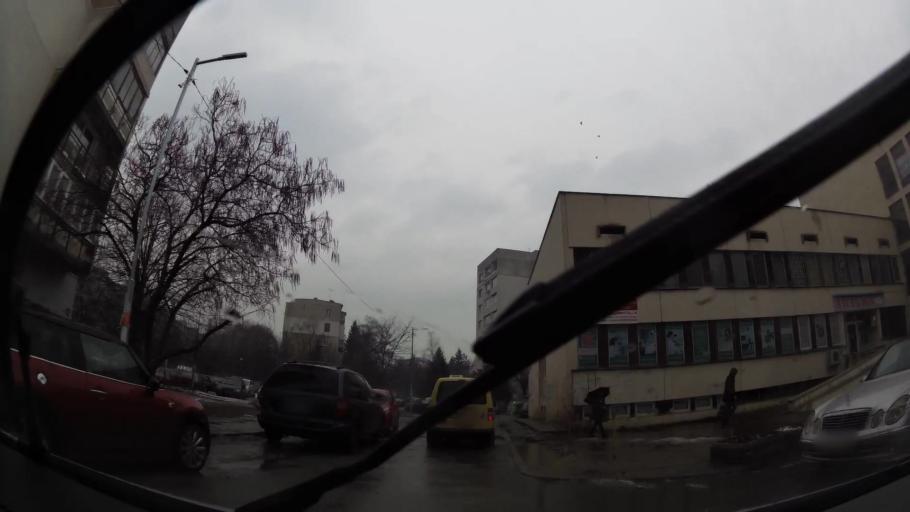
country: BG
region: Sofia-Capital
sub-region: Stolichna Obshtina
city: Sofia
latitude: 42.6644
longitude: 23.2967
